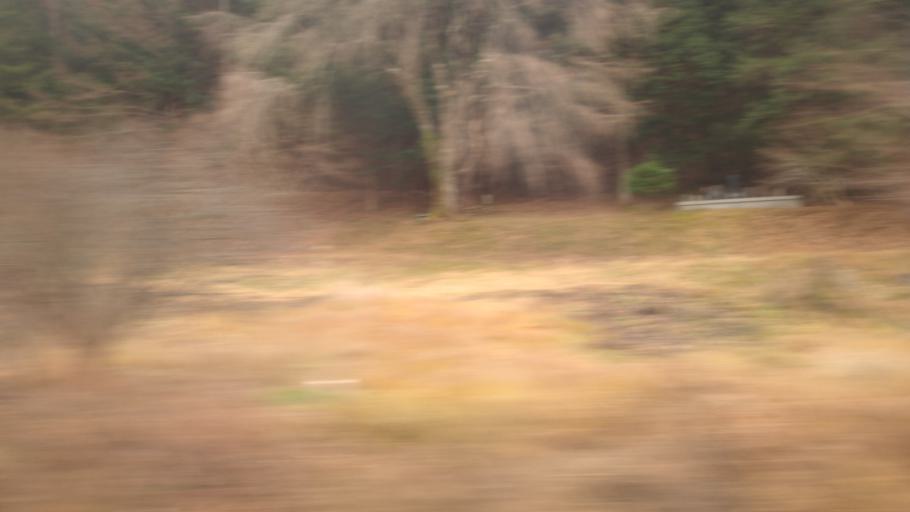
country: JP
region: Nagano
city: Ina
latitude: 35.8588
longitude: 137.7204
